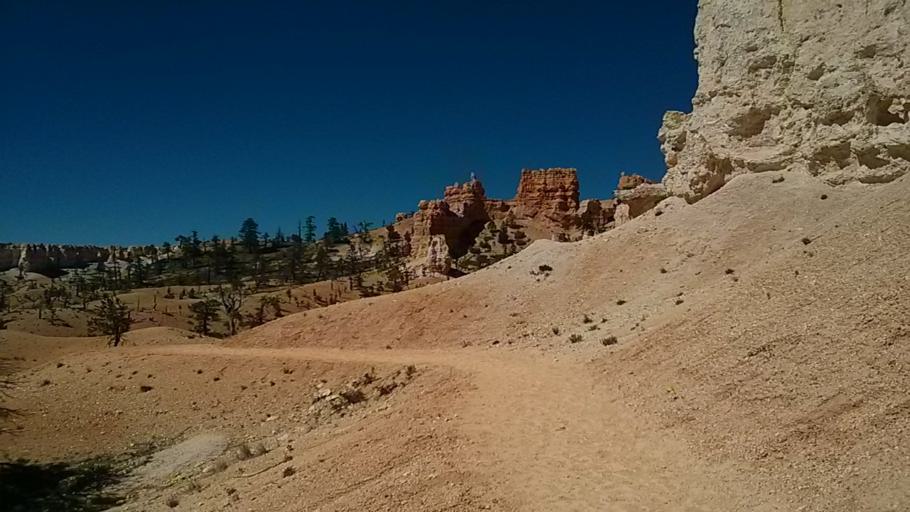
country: US
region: Utah
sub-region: Garfield County
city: Panguitch
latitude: 37.6363
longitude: -112.1524
